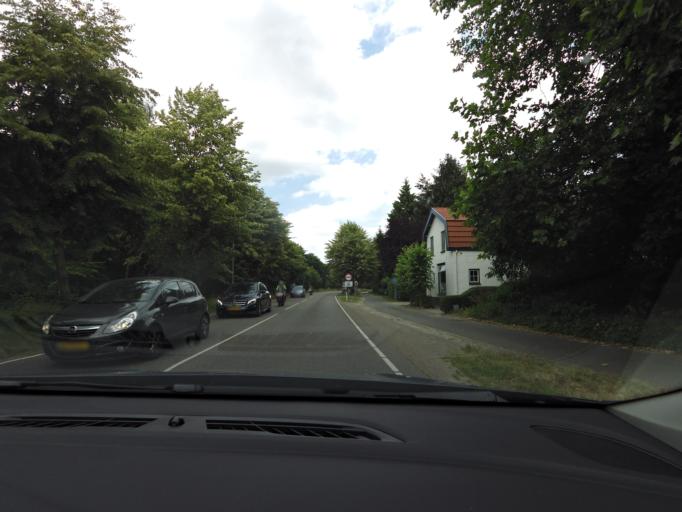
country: NL
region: North Brabant
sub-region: Gemeente Baarle-Nassau
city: Baarle-Nassau
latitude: 51.4496
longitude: 4.9164
